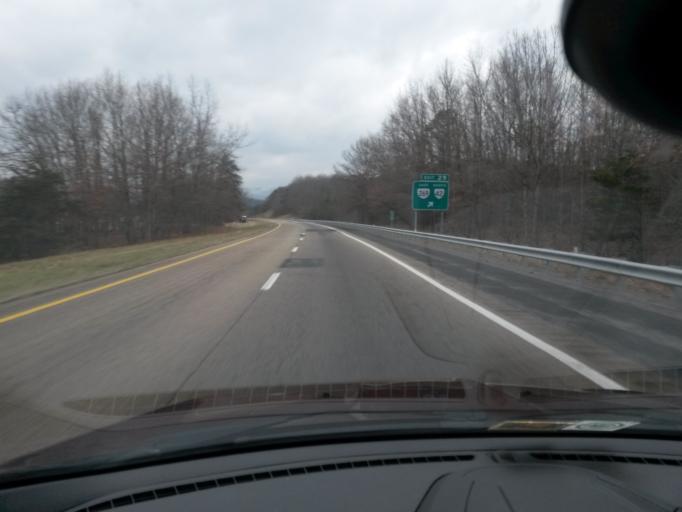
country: US
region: Virginia
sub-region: Alleghany County
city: Clifton Forge
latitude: 37.8289
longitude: -79.7531
